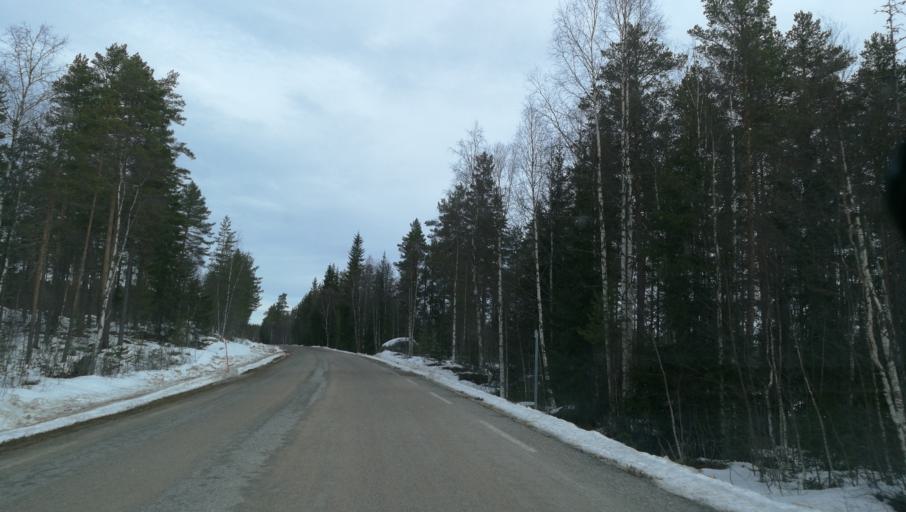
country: NO
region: Hedmark
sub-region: Grue
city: Kirkenaer
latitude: 60.5219
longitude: 12.5528
